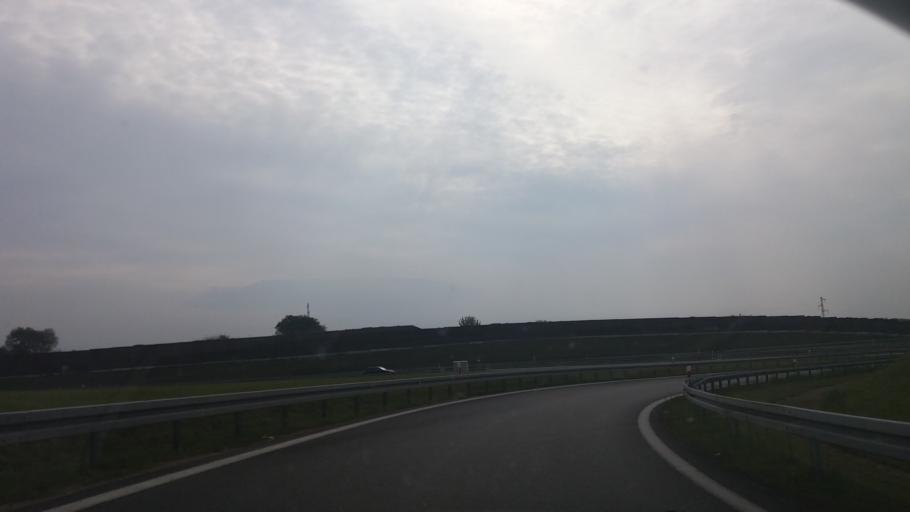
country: PL
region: Lesser Poland Voivodeship
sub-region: Powiat chrzanowski
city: Chrzanow
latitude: 50.1480
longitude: 19.4325
